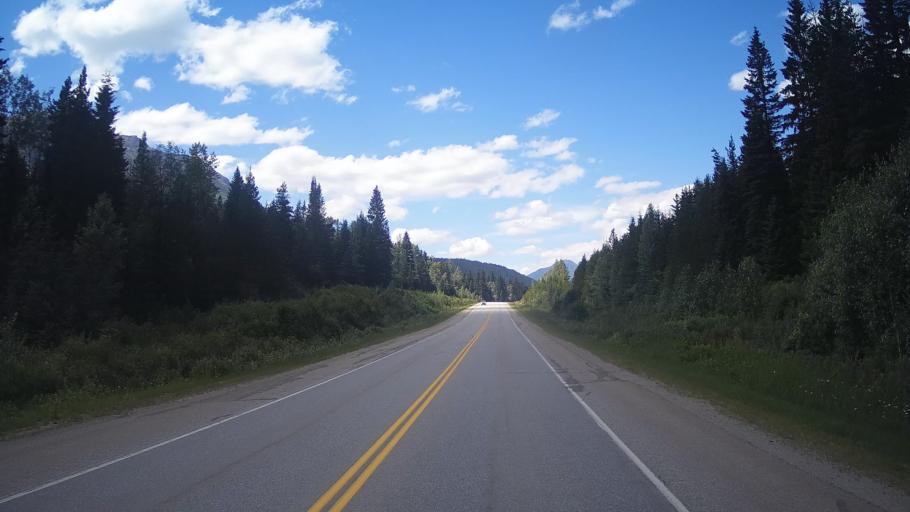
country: CA
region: Alberta
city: Grande Cache
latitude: 53.0019
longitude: -119.0384
